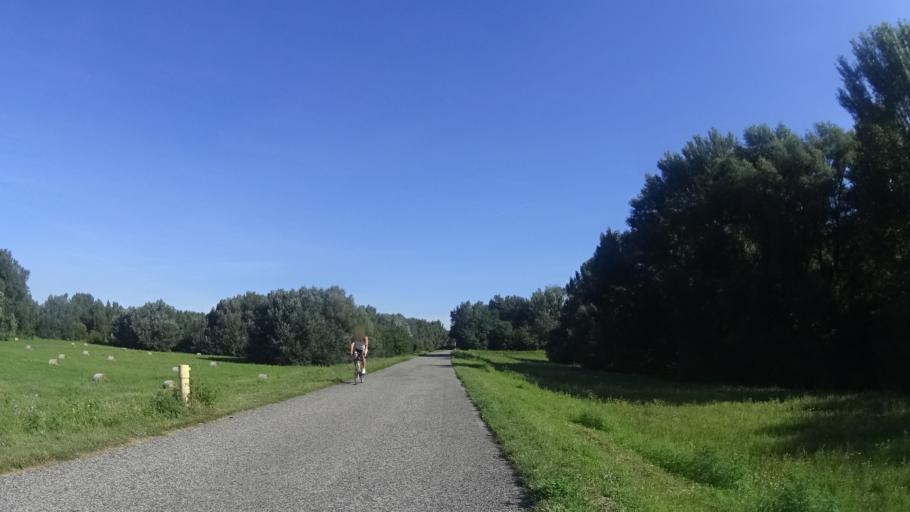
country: SK
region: Bratislavsky
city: Bratislava
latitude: 48.1093
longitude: 17.1463
